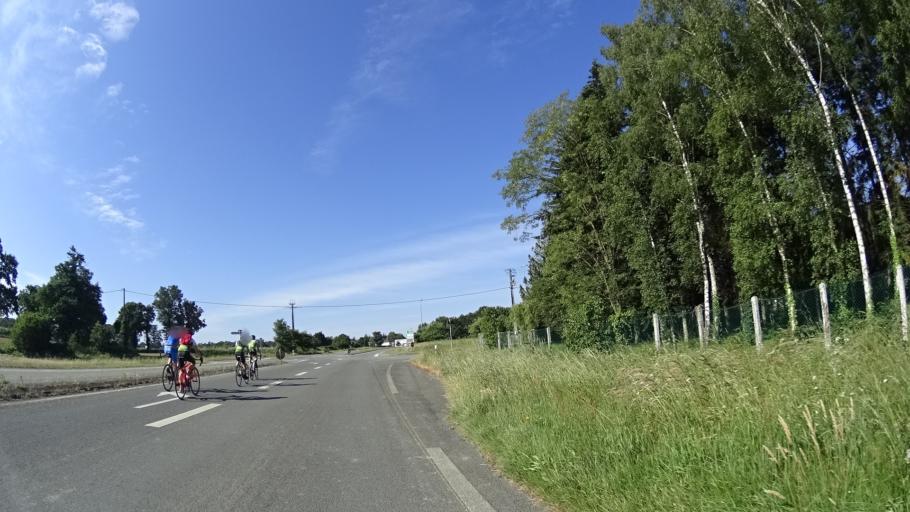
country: FR
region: Brittany
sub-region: Departement d'Ille-et-Vilaine
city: Guipry
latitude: 47.8656
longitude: -1.8783
